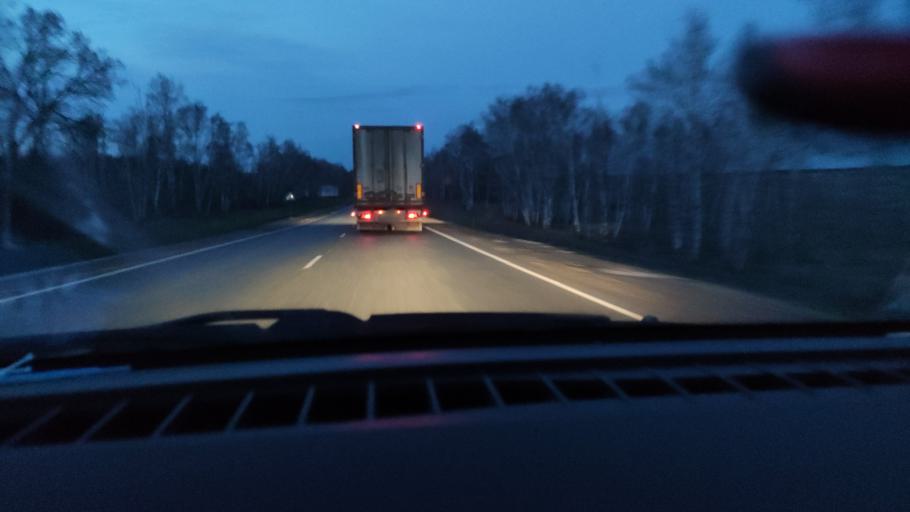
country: RU
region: Saratov
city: Sennoy
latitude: 52.1248
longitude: 46.8519
